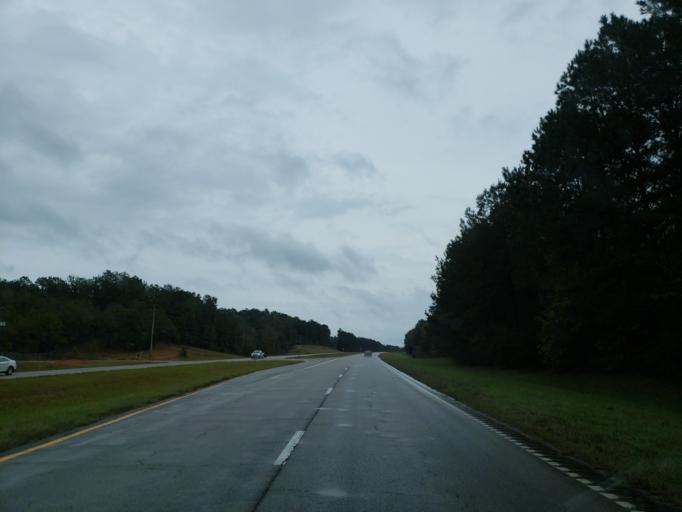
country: US
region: Mississippi
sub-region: Jones County
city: Laurel
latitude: 31.7058
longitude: -89.0683
